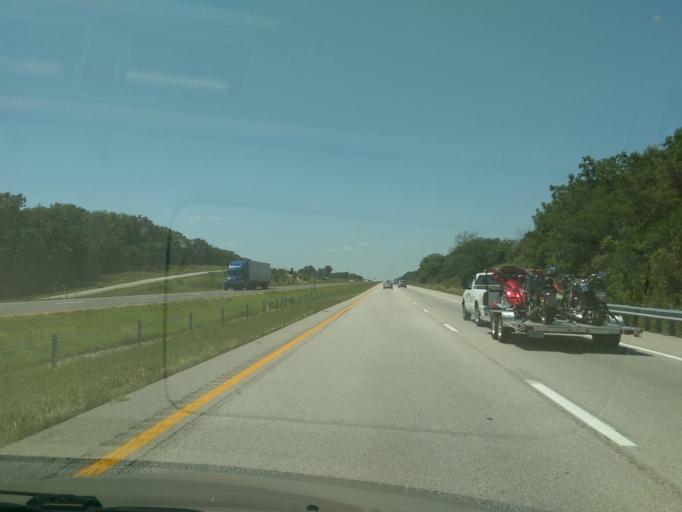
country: US
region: Missouri
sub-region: Saline County
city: Marshall
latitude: 38.9502
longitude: -93.0441
